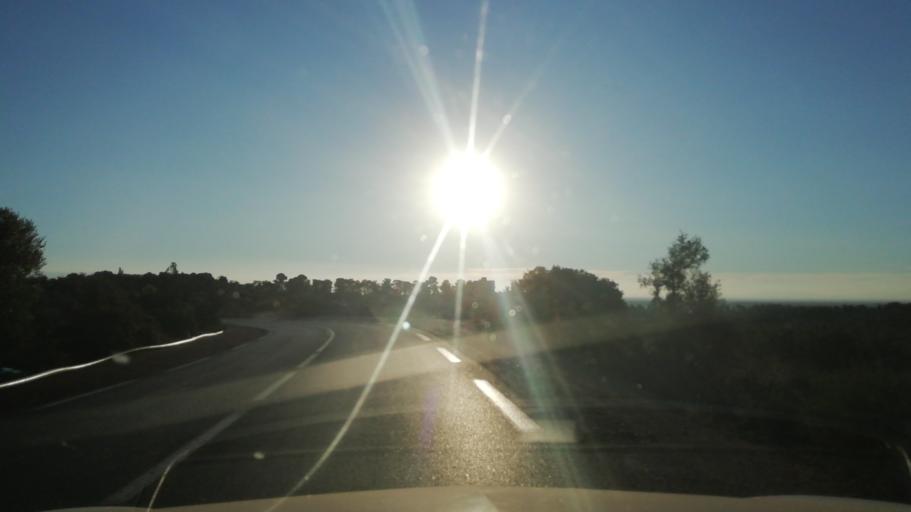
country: DZ
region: Tlemcen
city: Beni Mester
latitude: 34.8164
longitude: -1.6156
